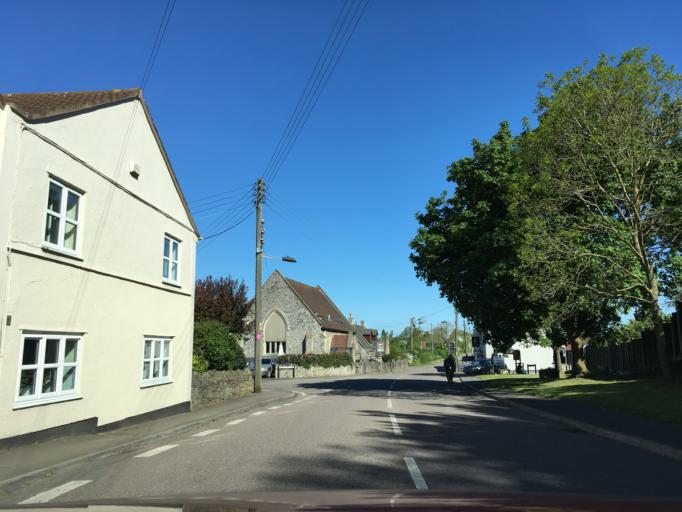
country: GB
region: England
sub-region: South Gloucestershire
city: Severn Beach
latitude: 51.5168
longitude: -2.6487
